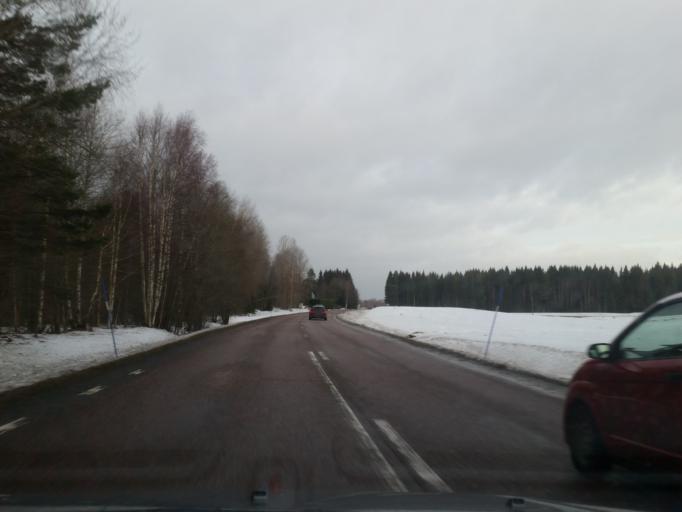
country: SE
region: Gaevleborg
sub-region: Sandvikens Kommun
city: Sandviken
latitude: 60.6649
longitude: 16.6923
